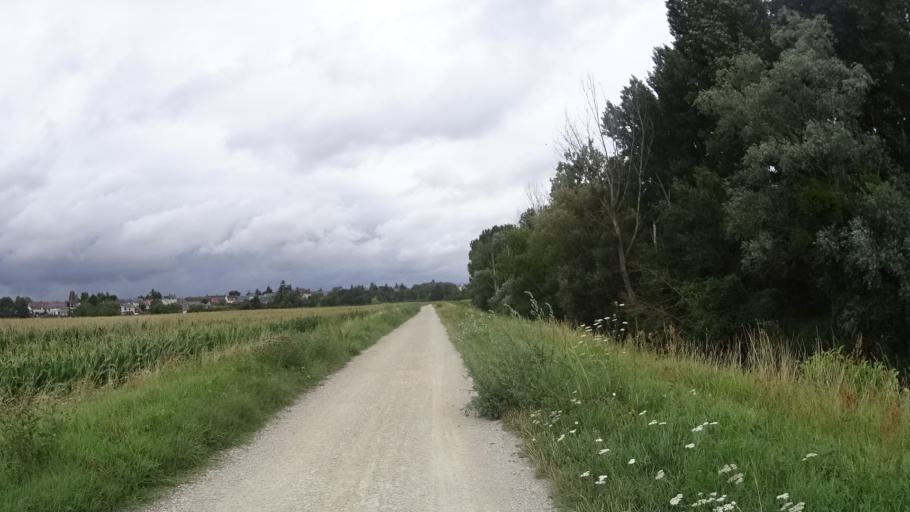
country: FR
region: Centre
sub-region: Departement du Loiret
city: Baule
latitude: 47.8083
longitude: 1.6833
